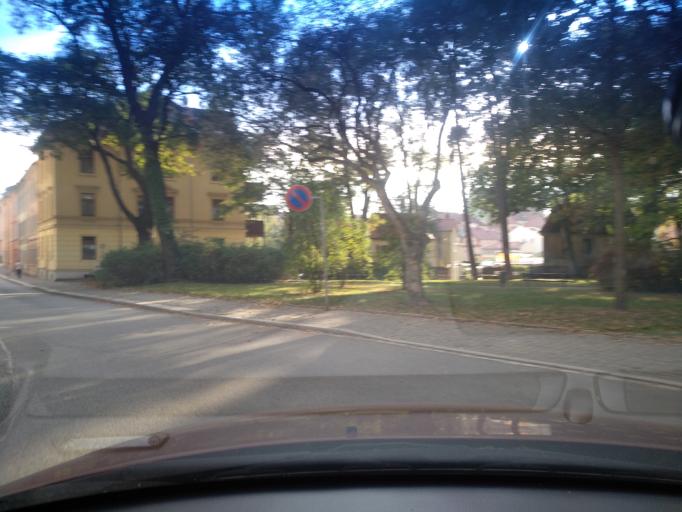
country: DE
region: Saxony
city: Bautzen
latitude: 51.1842
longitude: 14.4287
